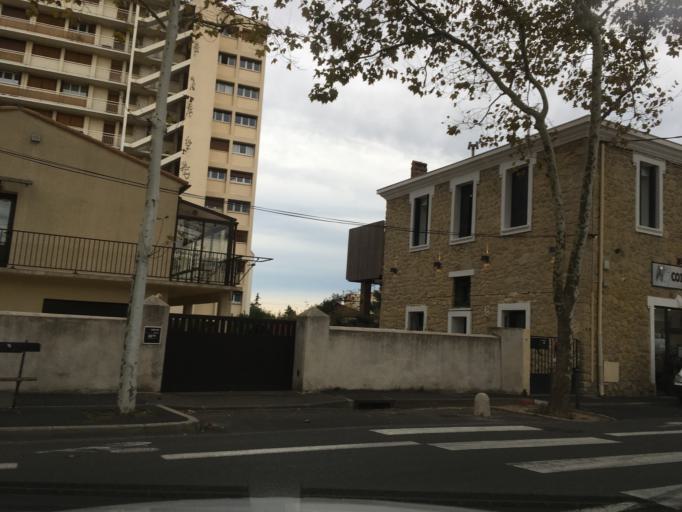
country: FR
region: Languedoc-Roussillon
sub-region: Departement de l'Herault
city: Montpellier
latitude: 43.6206
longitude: 3.8872
